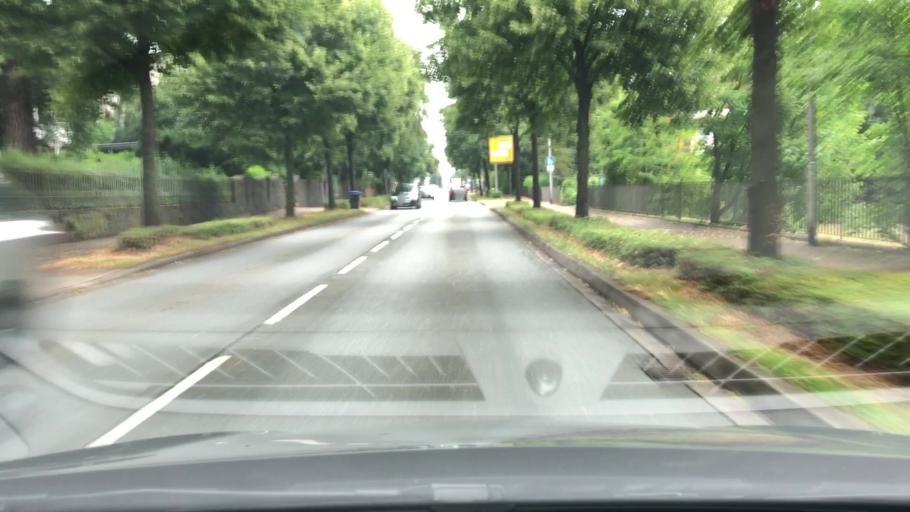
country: DE
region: North Rhine-Westphalia
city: Porta Westfalica
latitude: 52.2473
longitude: 8.9122
